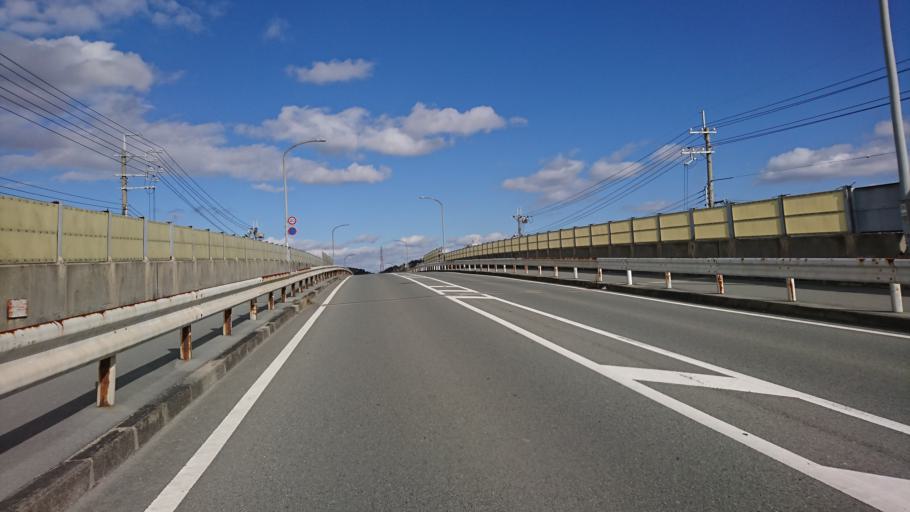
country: JP
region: Hyogo
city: Kakogawacho-honmachi
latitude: 34.7695
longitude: 134.7838
